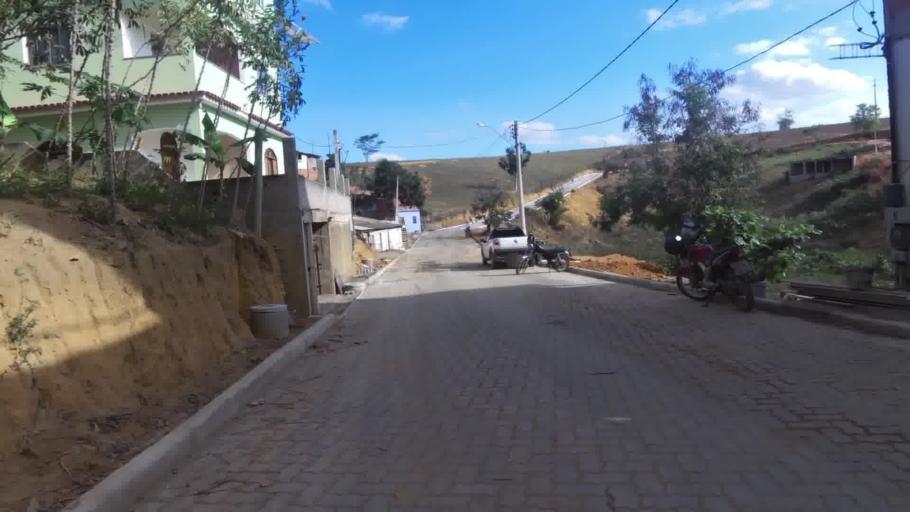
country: BR
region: Espirito Santo
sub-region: Marataizes
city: Marataizes
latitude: -21.1026
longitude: -41.0473
